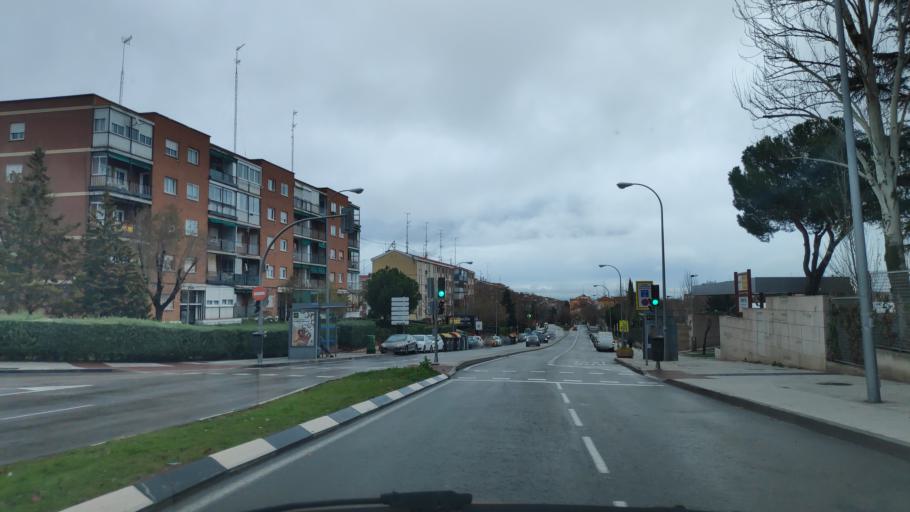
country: ES
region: Madrid
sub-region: Provincia de Madrid
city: Pinar de Chamartin
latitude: 40.4710
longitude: -3.6575
